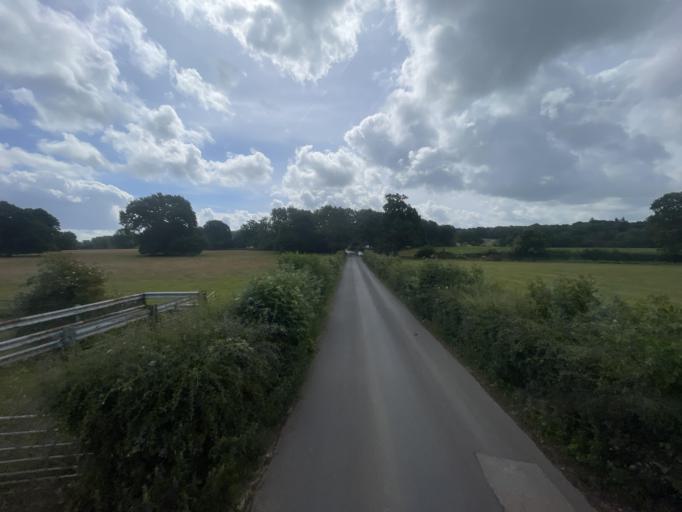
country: GB
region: England
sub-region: Kent
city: Edenbridge
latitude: 51.1582
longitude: 0.1492
